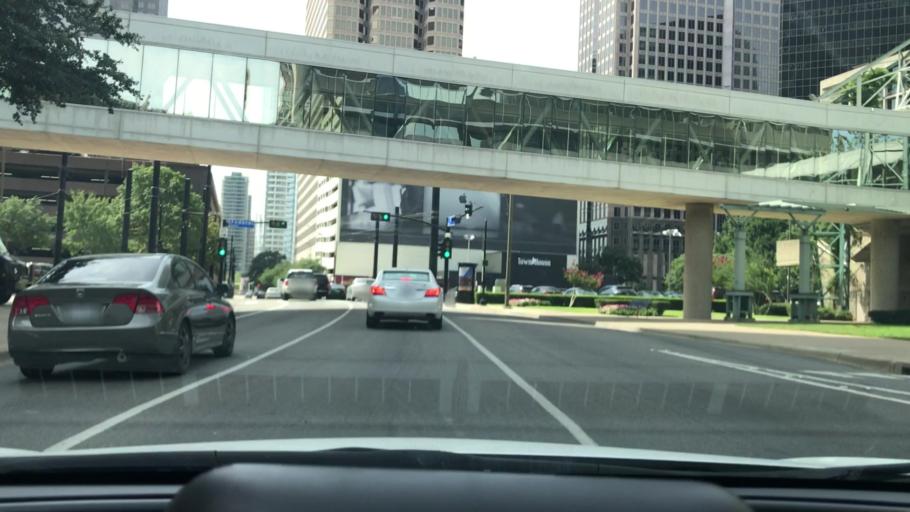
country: US
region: Texas
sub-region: Dallas County
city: Dallas
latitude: 32.7855
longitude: -96.7958
